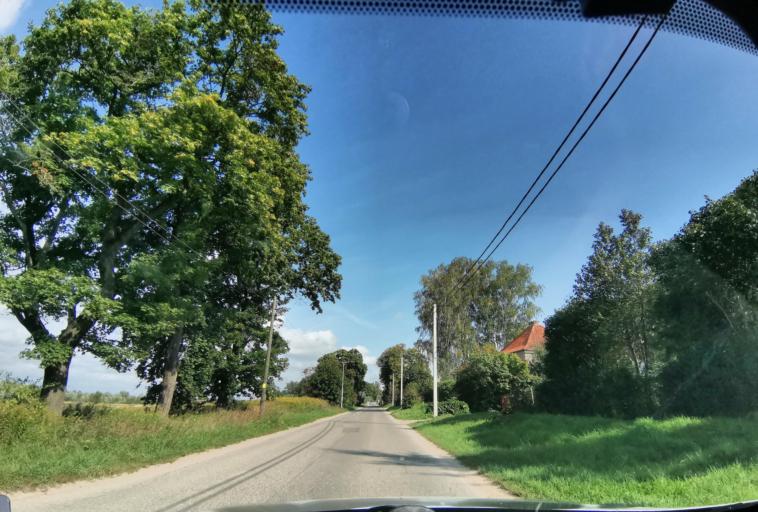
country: RU
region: Kaliningrad
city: Chernyakhovsk
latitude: 54.6552
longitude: 21.8228
